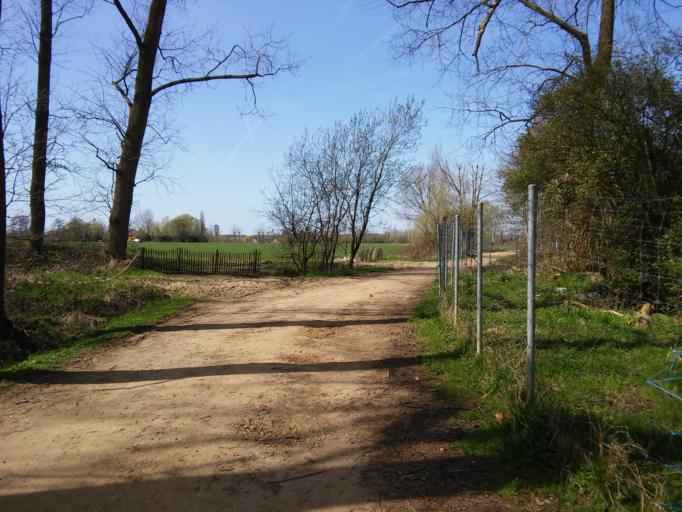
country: BE
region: Flanders
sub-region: Provincie Antwerpen
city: Rumst
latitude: 51.0933
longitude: 4.4012
